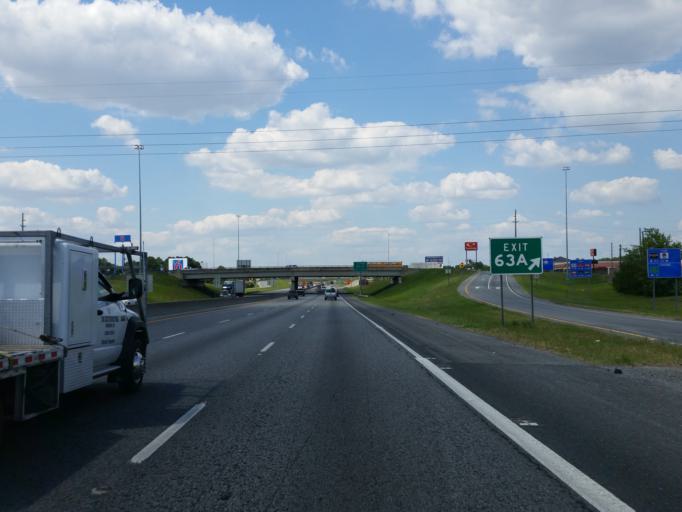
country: US
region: Georgia
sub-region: Tift County
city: Tifton
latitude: 31.4560
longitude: -83.5302
